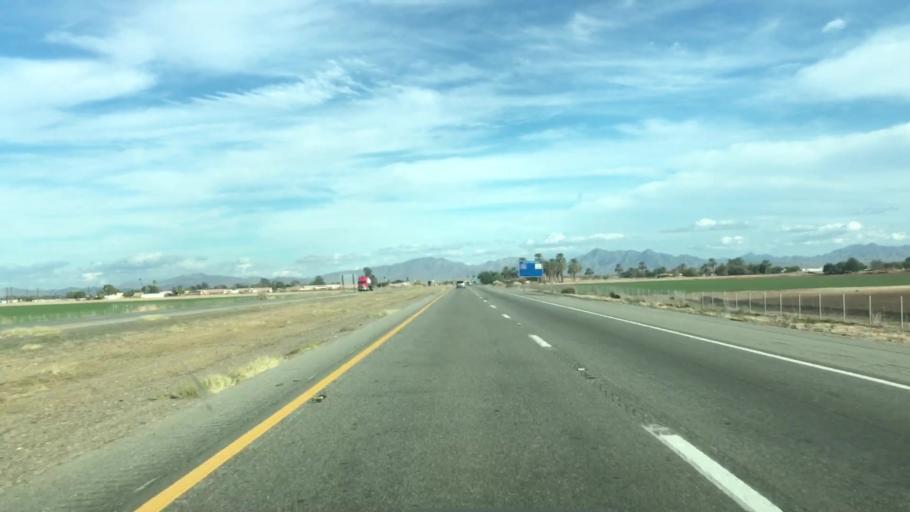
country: US
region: California
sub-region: Riverside County
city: Blythe
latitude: 33.6065
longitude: -114.6371
